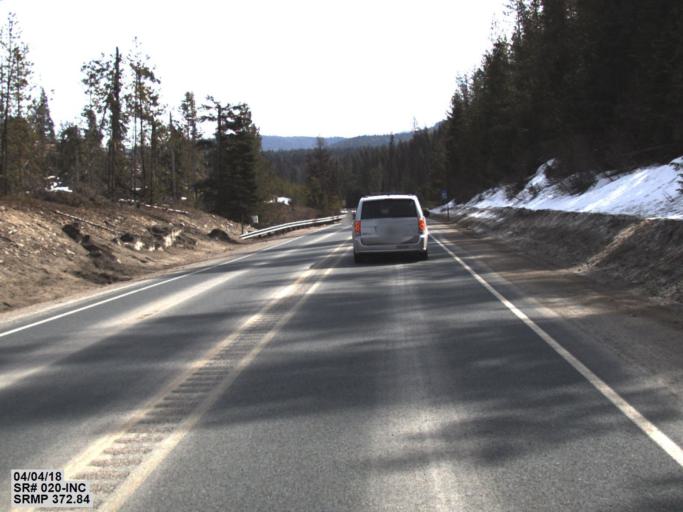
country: US
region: Washington
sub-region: Stevens County
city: Chewelah
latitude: 48.5400
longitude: -117.5966
